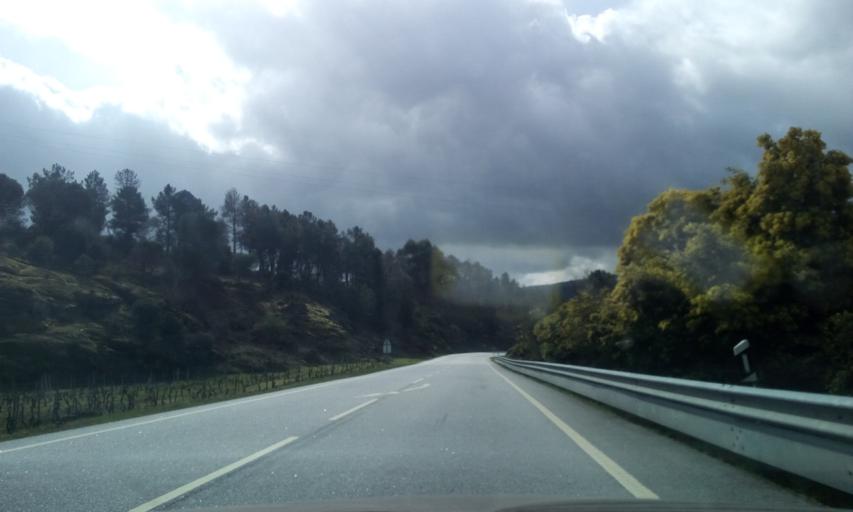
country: PT
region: Viseu
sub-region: Mangualde
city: Mangualde
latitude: 40.6524
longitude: -7.7332
